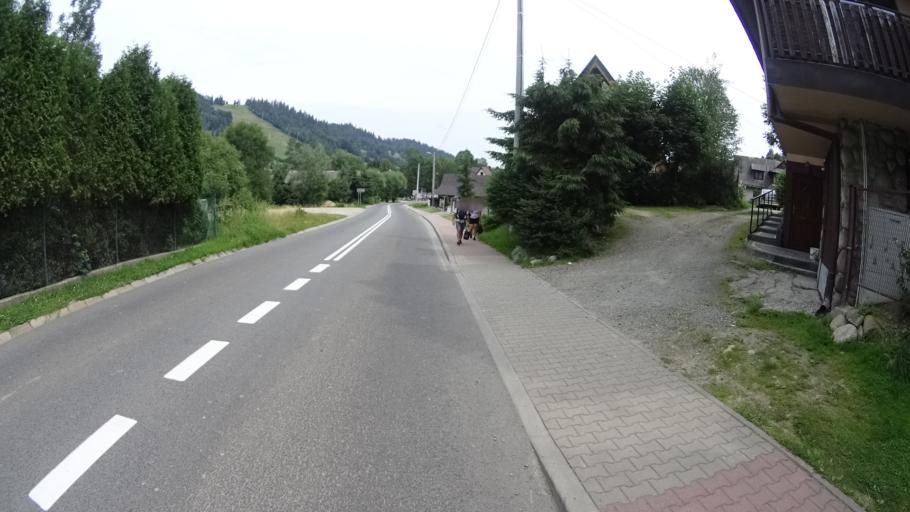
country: PL
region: Lesser Poland Voivodeship
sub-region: Powiat tatrzanski
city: Zakopane
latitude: 49.3145
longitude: 19.9771
